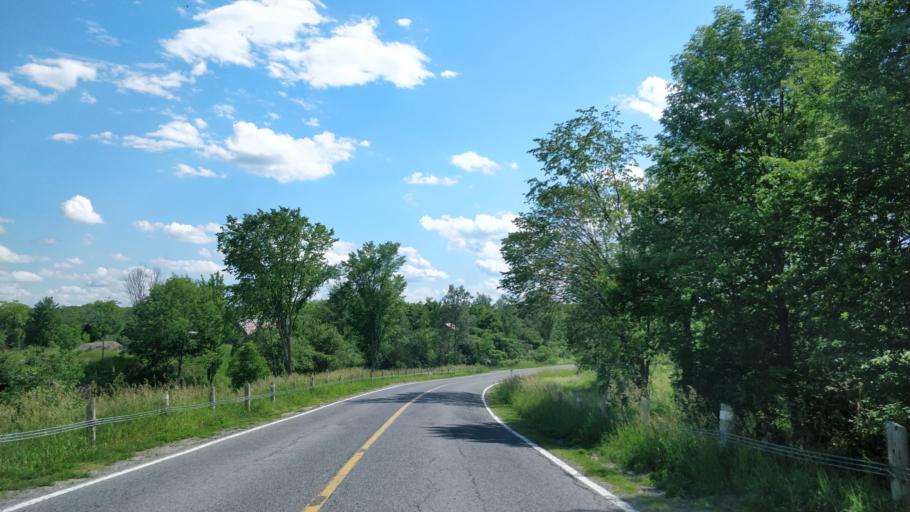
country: CA
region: Ontario
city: Perth
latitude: 44.7415
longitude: -76.4982
